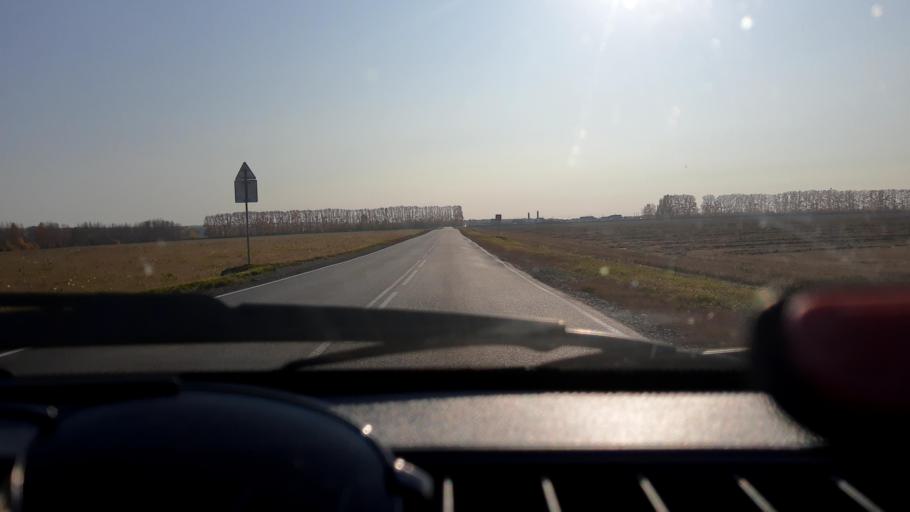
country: RU
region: Bashkortostan
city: Kabakovo
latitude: 54.4739
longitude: 55.9565
